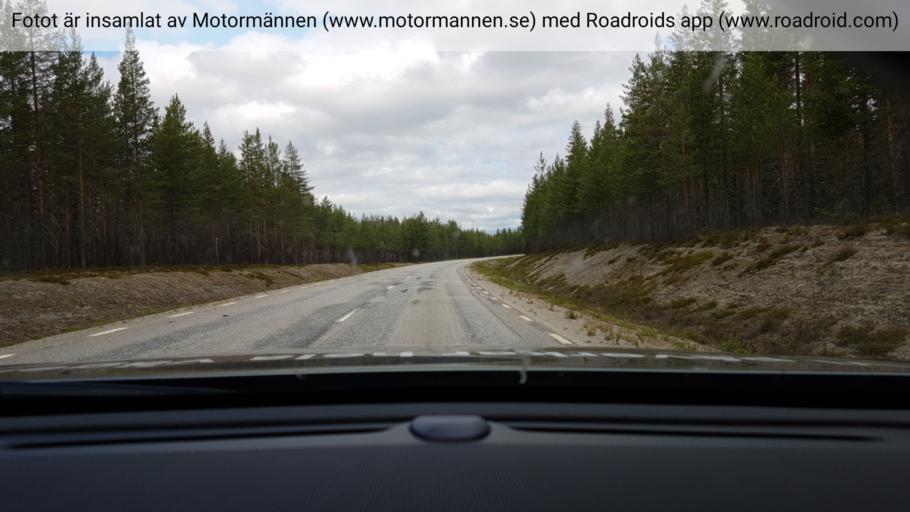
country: SE
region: Vaesterbotten
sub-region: Mala Kommun
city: Mala
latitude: 64.9205
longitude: 18.6254
